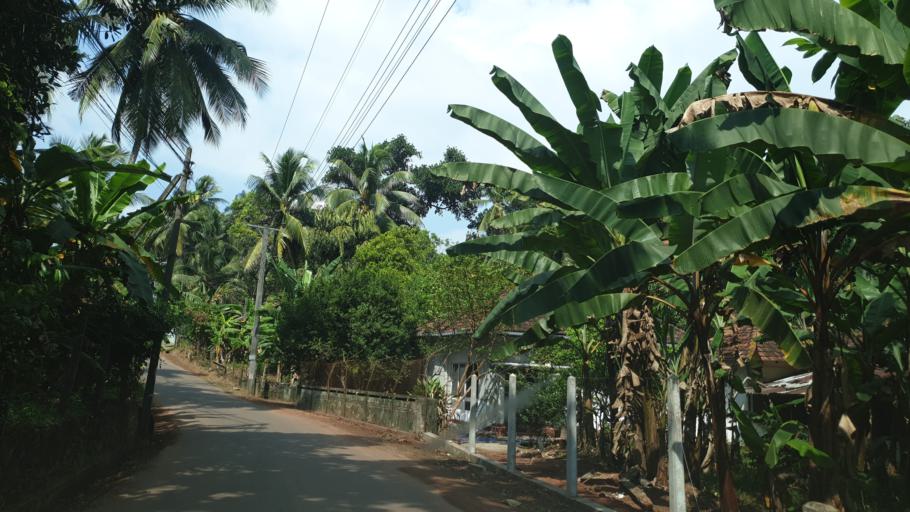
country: LK
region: Western
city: Panadura
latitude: 6.7242
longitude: 79.9542
